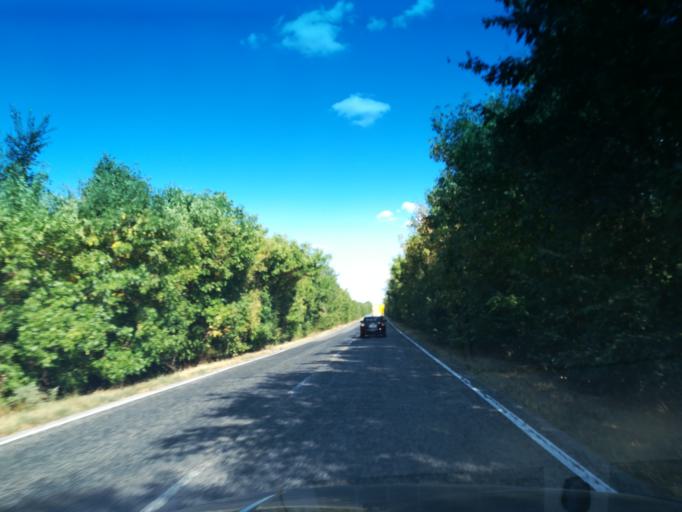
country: BG
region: Khaskovo
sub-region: Obshtina Mineralni Bani
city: Mineralni Bani
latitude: 42.0542
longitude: 25.3116
